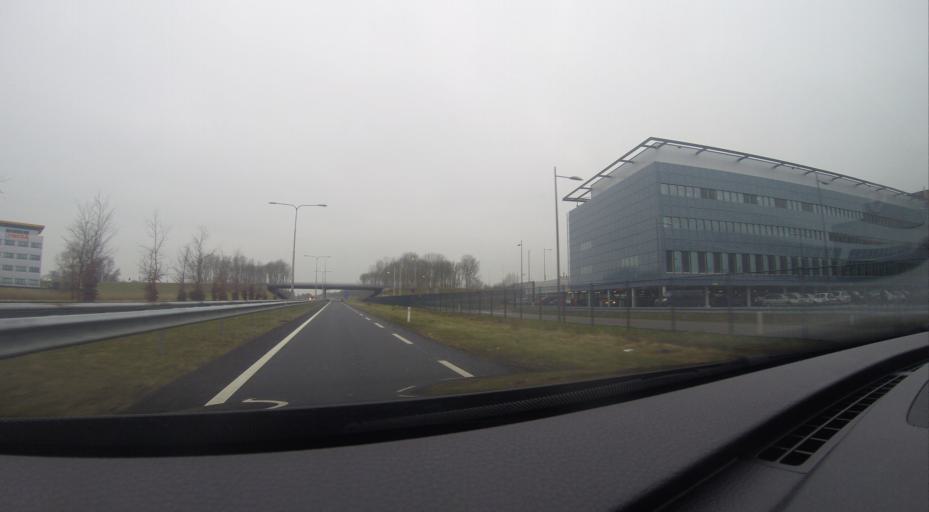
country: NL
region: Gelderland
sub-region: Gemeente Zutphen
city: Leesten
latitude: 52.1221
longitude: 6.2182
